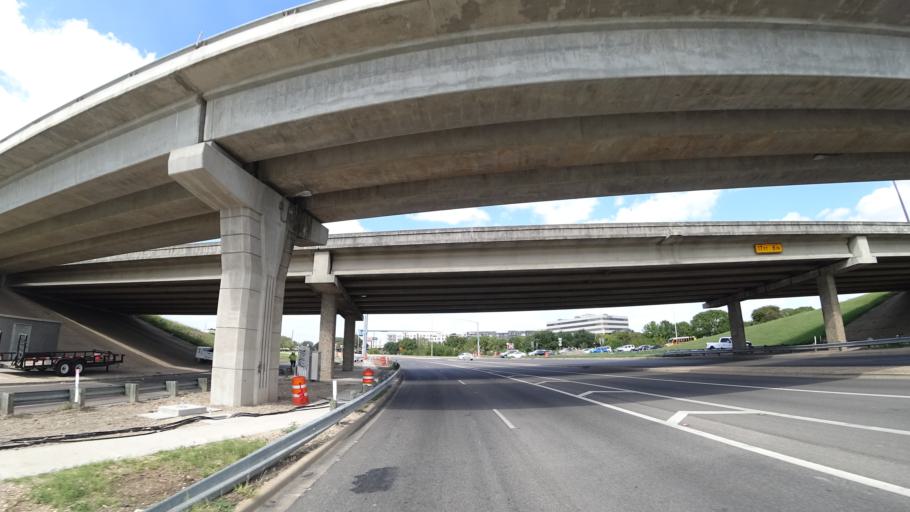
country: US
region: Texas
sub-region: Travis County
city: Austin
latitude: 30.3202
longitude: -97.7127
